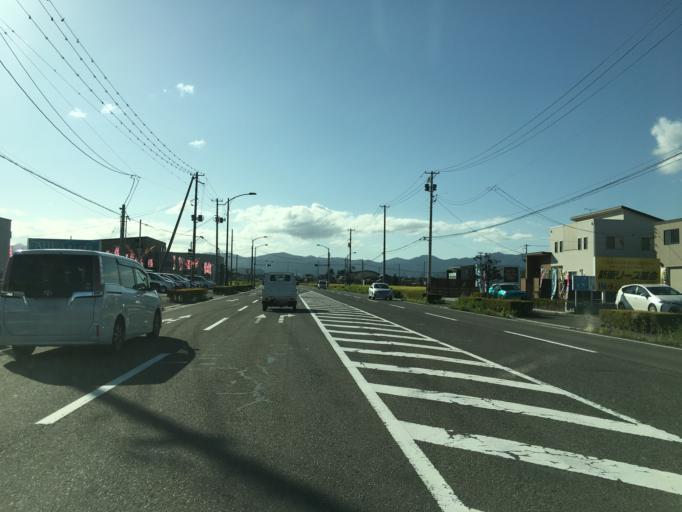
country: JP
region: Fukushima
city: Koriyama
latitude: 37.3861
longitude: 140.3261
